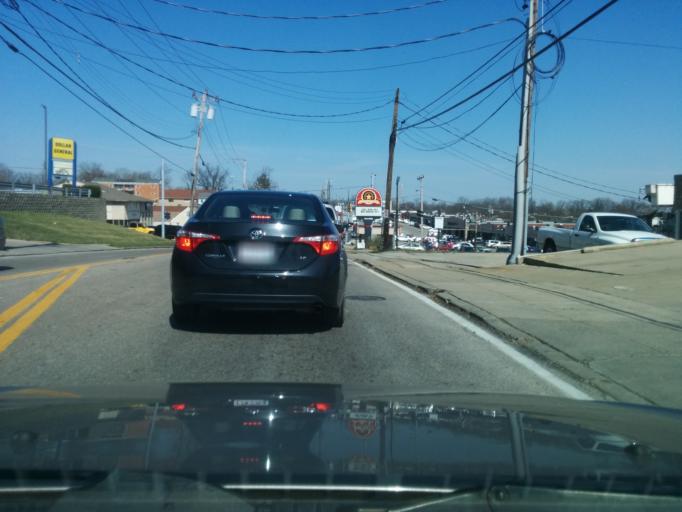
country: US
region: Ohio
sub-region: Hamilton County
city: Monfort Heights
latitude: 39.1980
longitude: -84.6011
